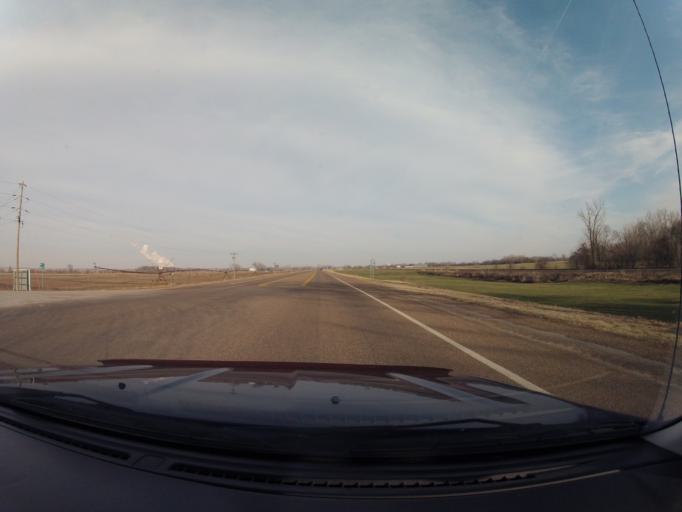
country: US
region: Kansas
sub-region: Pottawatomie County
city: Wamego
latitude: 39.2142
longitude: -96.2313
